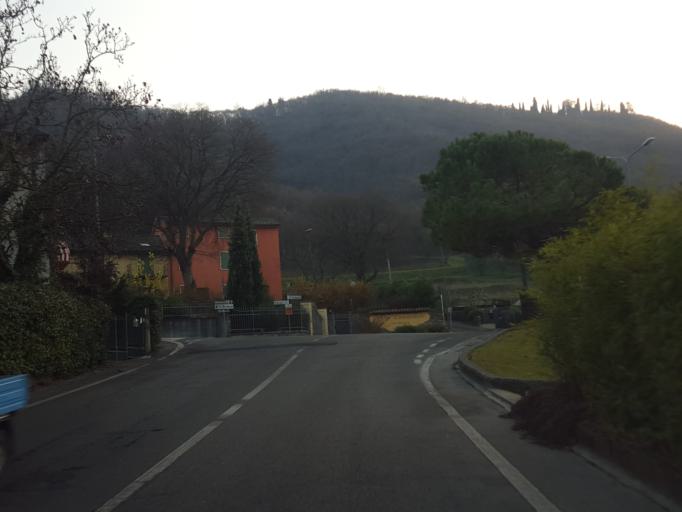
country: IT
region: Veneto
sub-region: Provincia di Verona
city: Garda
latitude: 45.5756
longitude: 10.7260
